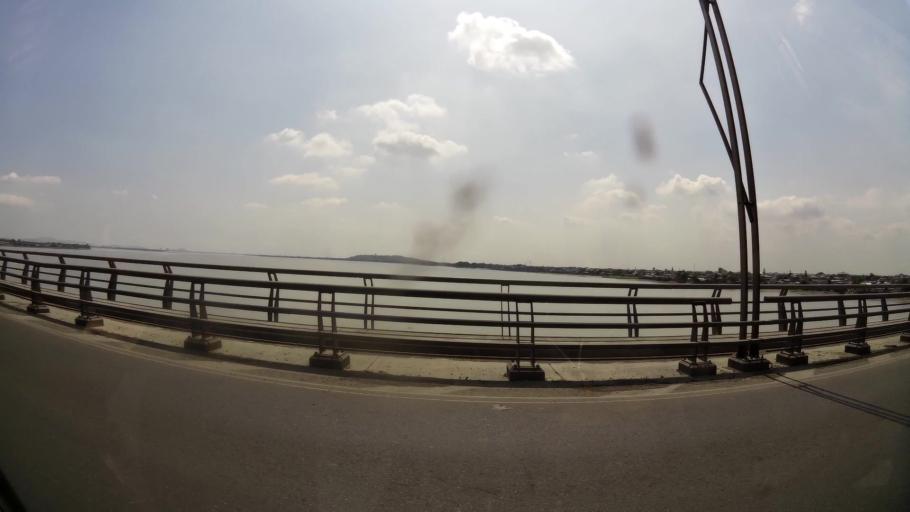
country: EC
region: Guayas
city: Eloy Alfaro
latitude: -2.1629
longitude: -79.8482
